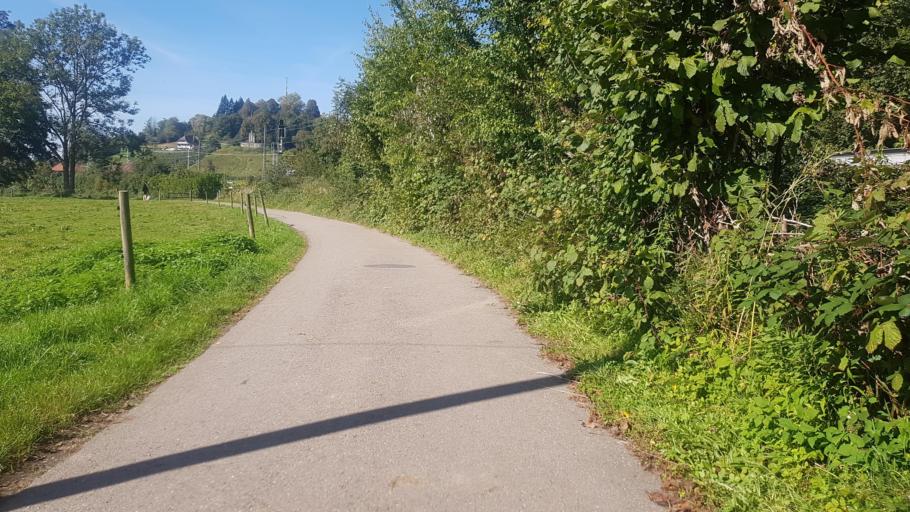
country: DE
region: Bavaria
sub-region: Swabia
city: Bodolz
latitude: 47.5621
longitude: 9.6813
